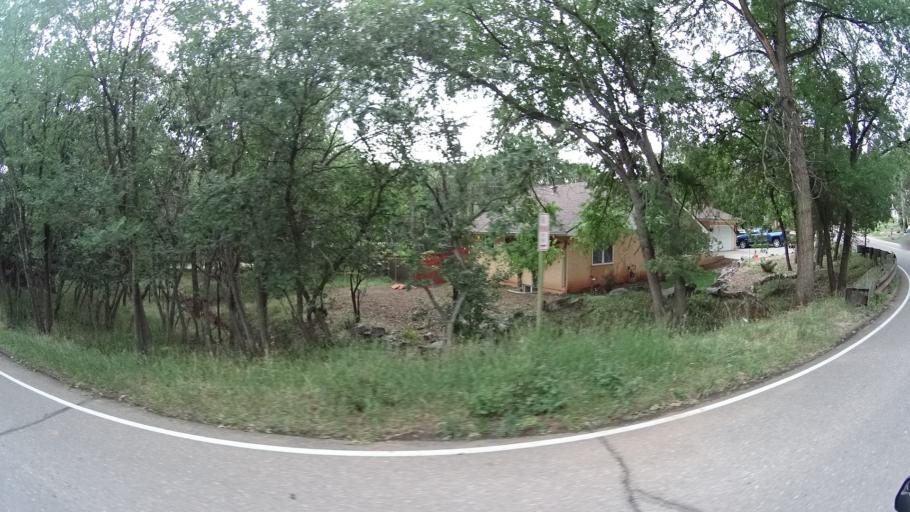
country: US
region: Colorado
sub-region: El Paso County
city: Manitou Springs
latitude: 38.8516
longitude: -104.8978
